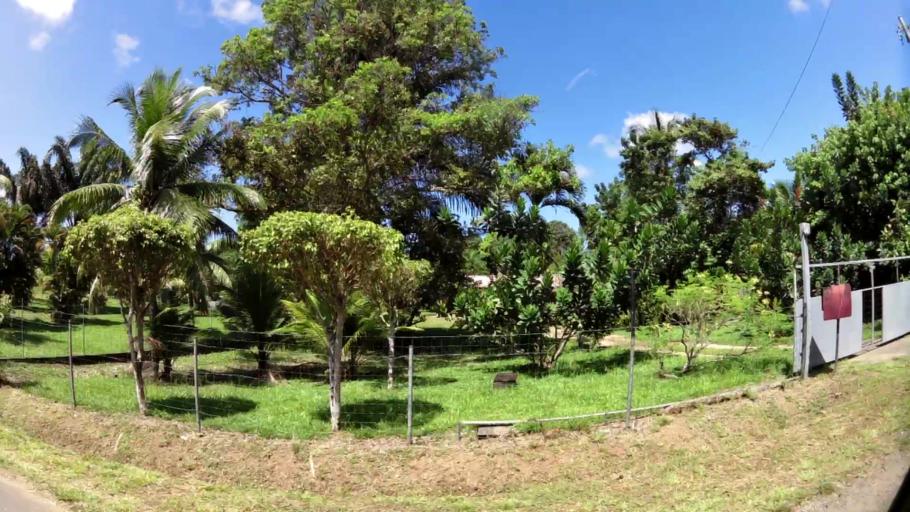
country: GF
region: Guyane
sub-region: Guyane
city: Matoury
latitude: 4.8329
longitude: -52.3231
